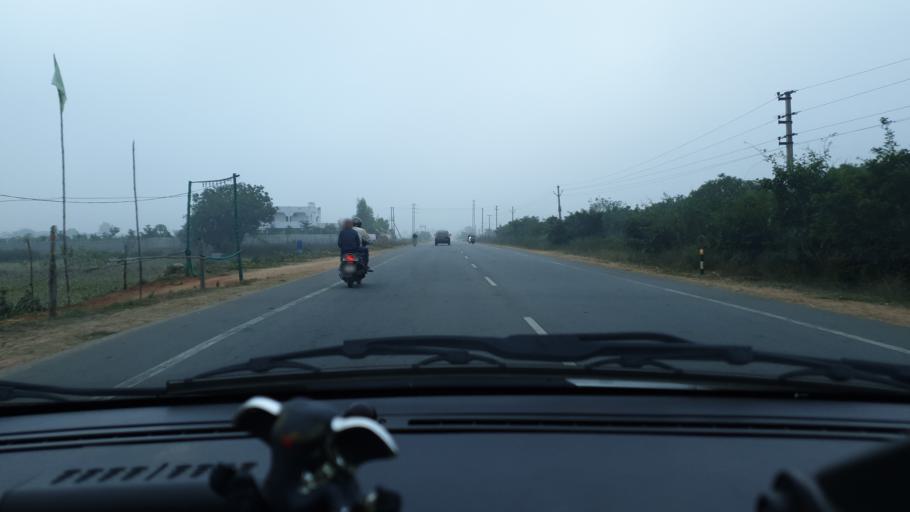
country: IN
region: Telangana
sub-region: Mahbubnagar
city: Farrukhnagar
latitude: 16.9348
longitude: 78.5287
